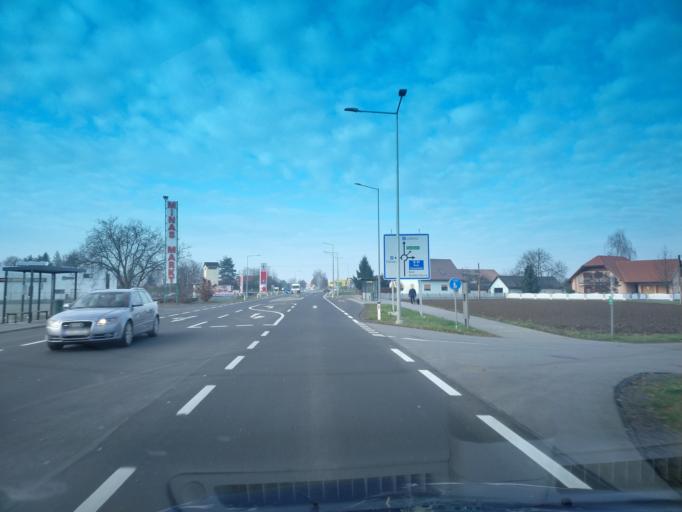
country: AT
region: Styria
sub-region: Politischer Bezirk Leibnitz
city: Sankt Veit am Vogau
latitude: 46.7393
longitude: 15.6060
